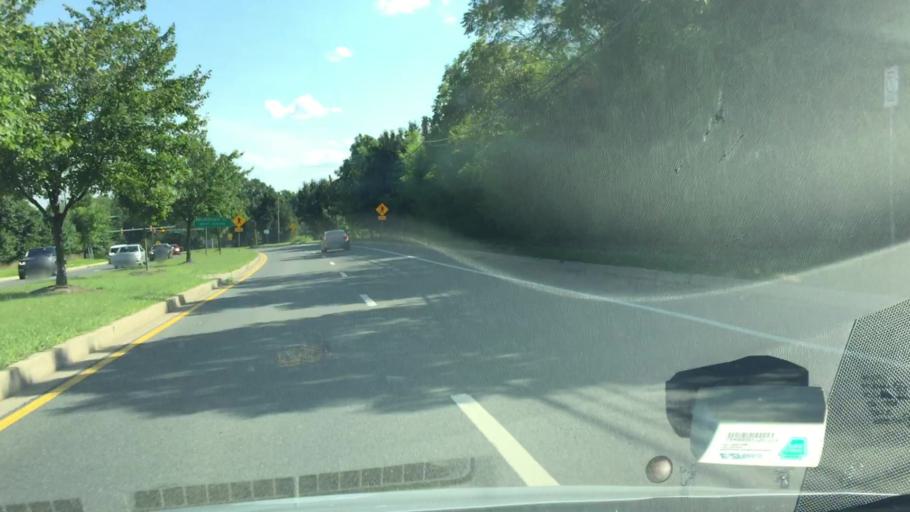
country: US
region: Maryland
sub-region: Montgomery County
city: Layhill
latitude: 39.0830
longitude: -77.0468
